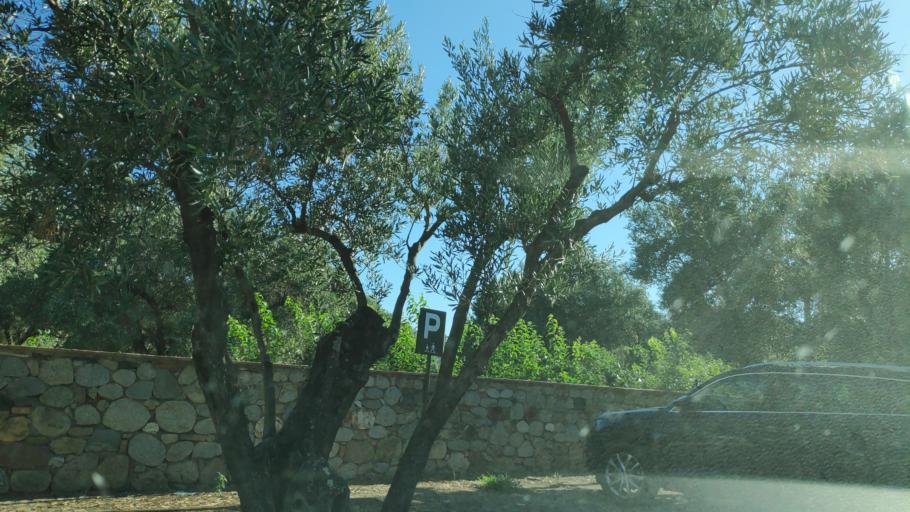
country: IT
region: Calabria
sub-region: Provincia di Catanzaro
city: Roccelletta
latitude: 38.8098
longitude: 16.5971
